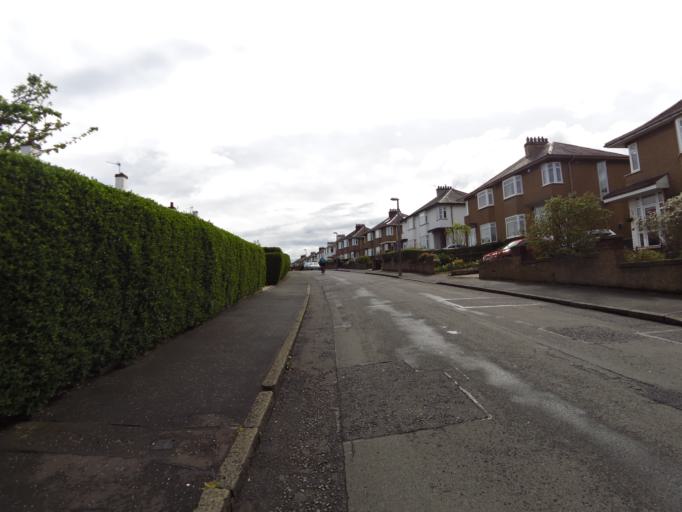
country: GB
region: Scotland
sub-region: Edinburgh
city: Colinton
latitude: 55.9674
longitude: -3.2717
